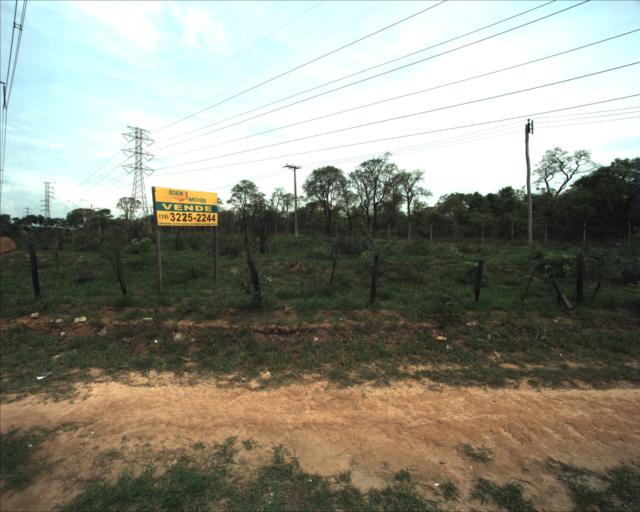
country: BR
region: Sao Paulo
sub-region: Sorocaba
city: Sorocaba
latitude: -23.4255
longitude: -47.4209
